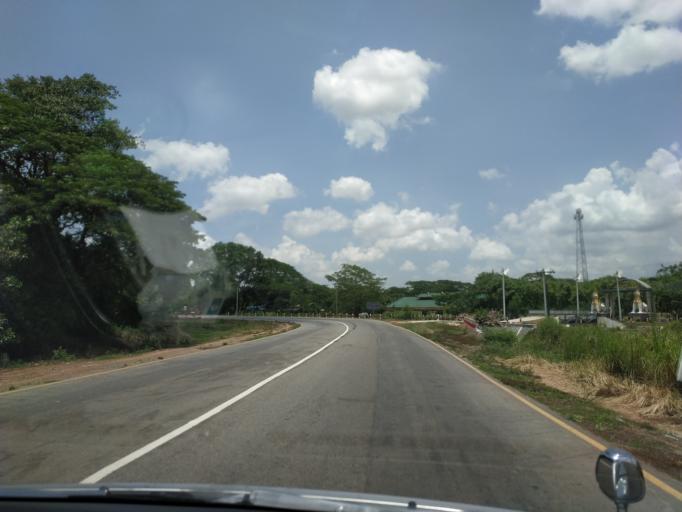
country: MM
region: Bago
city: Thanatpin
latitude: 17.4479
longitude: 96.6254
